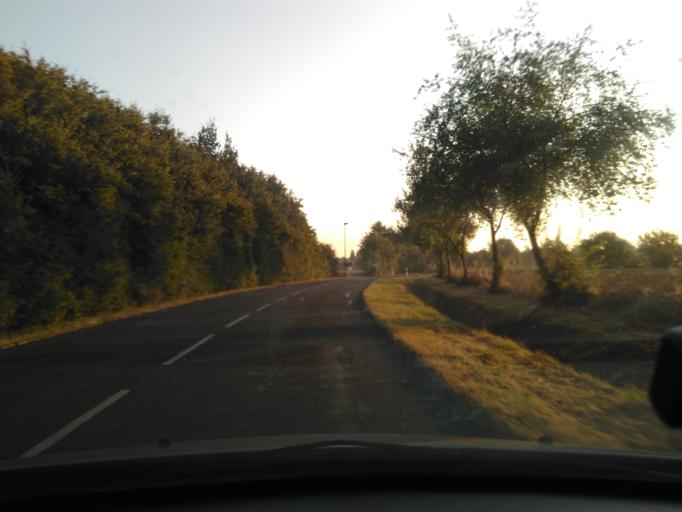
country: FR
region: Pays de la Loire
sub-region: Departement de la Vendee
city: Les Brouzils
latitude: 46.8788
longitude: -1.3187
